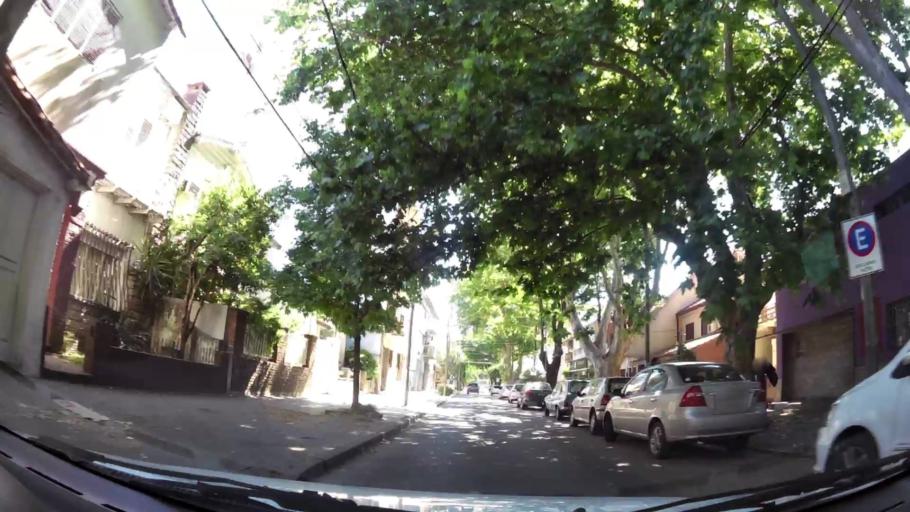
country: AR
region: Buenos Aires
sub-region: Partido de Vicente Lopez
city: Olivos
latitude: -34.5192
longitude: -58.4883
